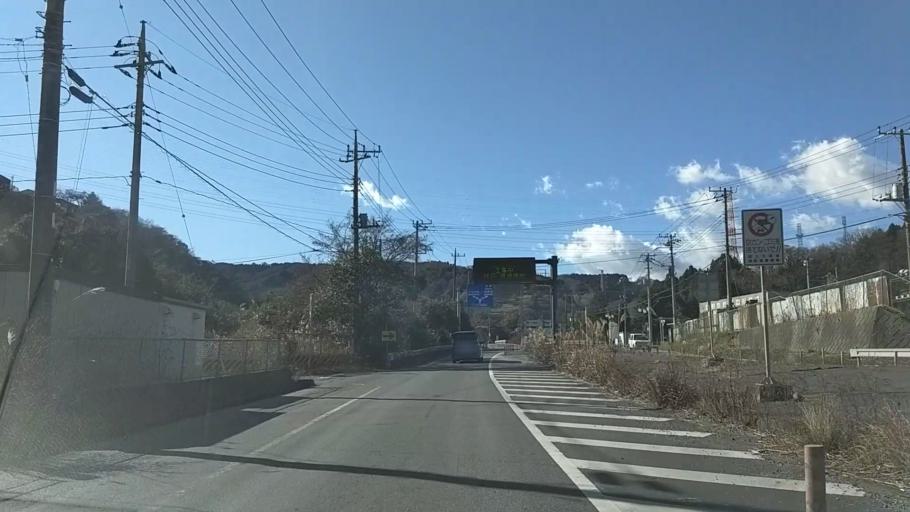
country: JP
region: Shizuoka
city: Gotemba
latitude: 35.3593
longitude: 139.0118
